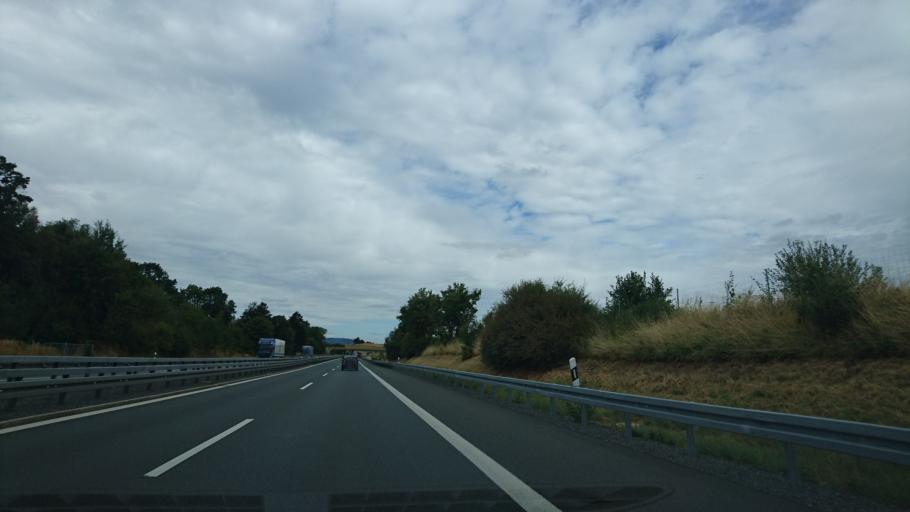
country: DE
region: Bavaria
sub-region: Upper Franconia
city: Thierstein
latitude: 50.0865
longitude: 12.1030
